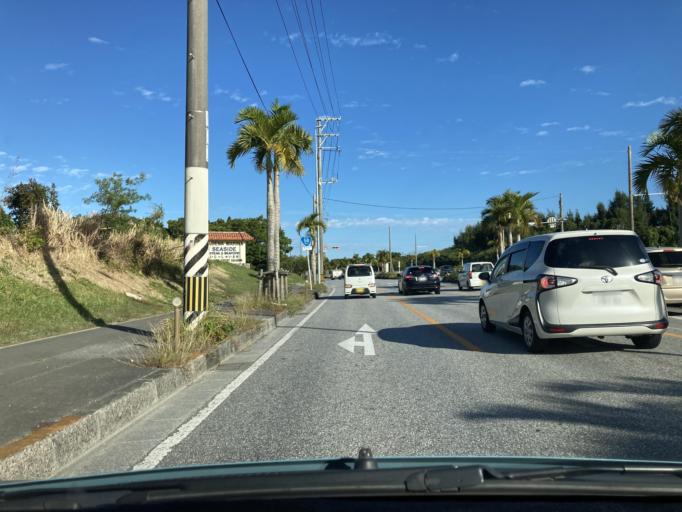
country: JP
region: Okinawa
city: Chatan
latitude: 26.3496
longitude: 127.7468
